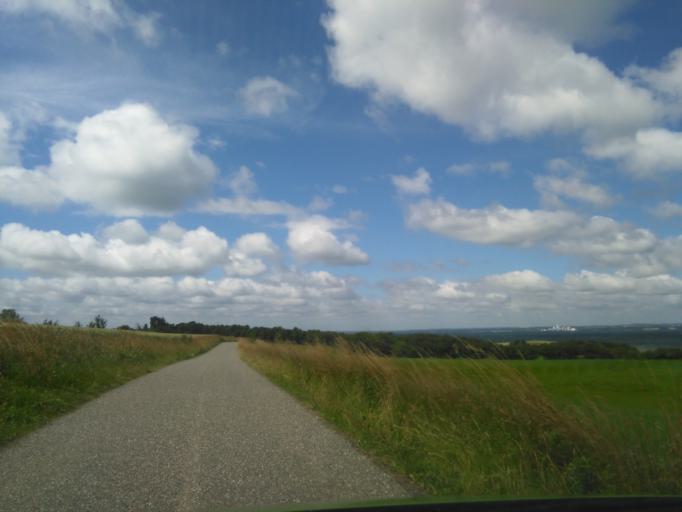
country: DK
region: Central Jutland
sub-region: Syddjurs Kommune
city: Ronde
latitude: 56.2392
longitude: 10.4783
